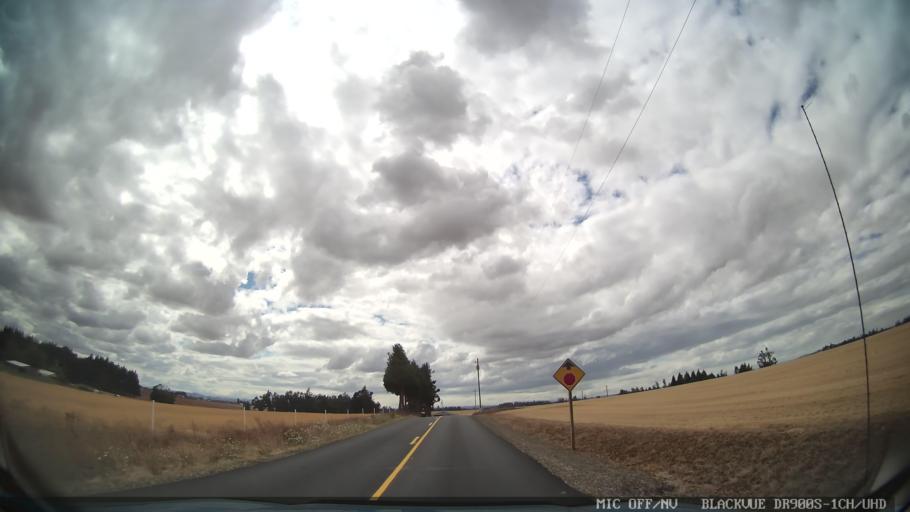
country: US
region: Oregon
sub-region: Marion County
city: Sublimity
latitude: 44.8406
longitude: -122.7919
